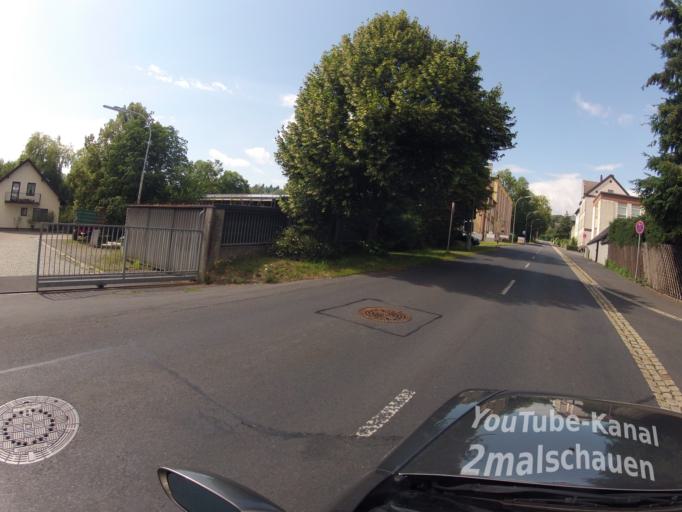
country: DE
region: Bavaria
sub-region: Upper Franconia
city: Wunsiedel
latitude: 50.0411
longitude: 11.9968
